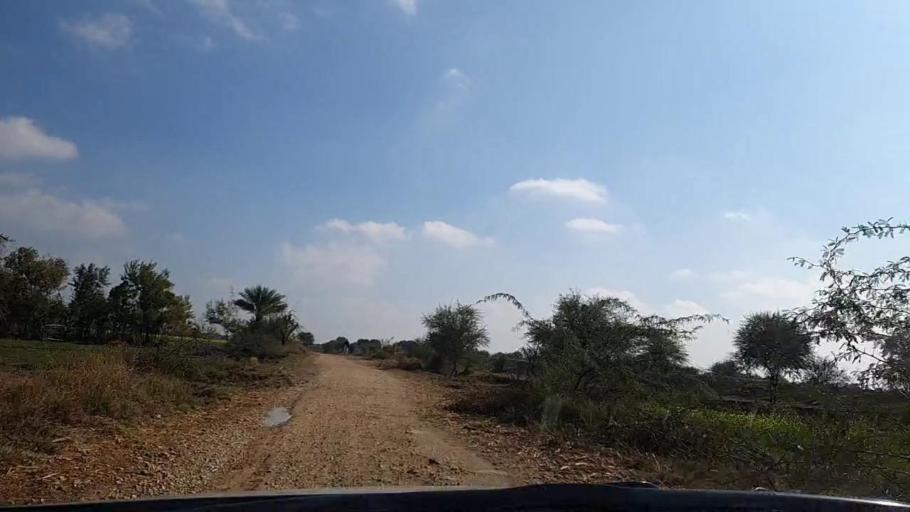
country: PK
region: Sindh
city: Tando Mittha Khan
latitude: 25.7405
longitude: 69.2409
